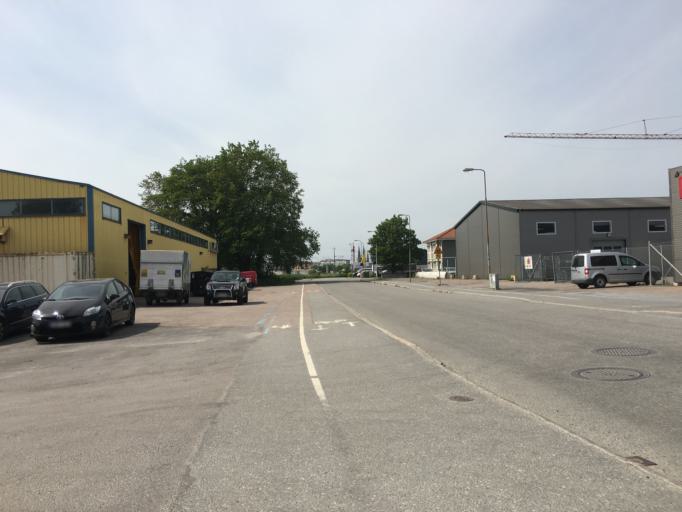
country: SE
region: Uppsala
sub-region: Uppsala Kommun
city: Uppsala
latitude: 59.8476
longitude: 17.6688
